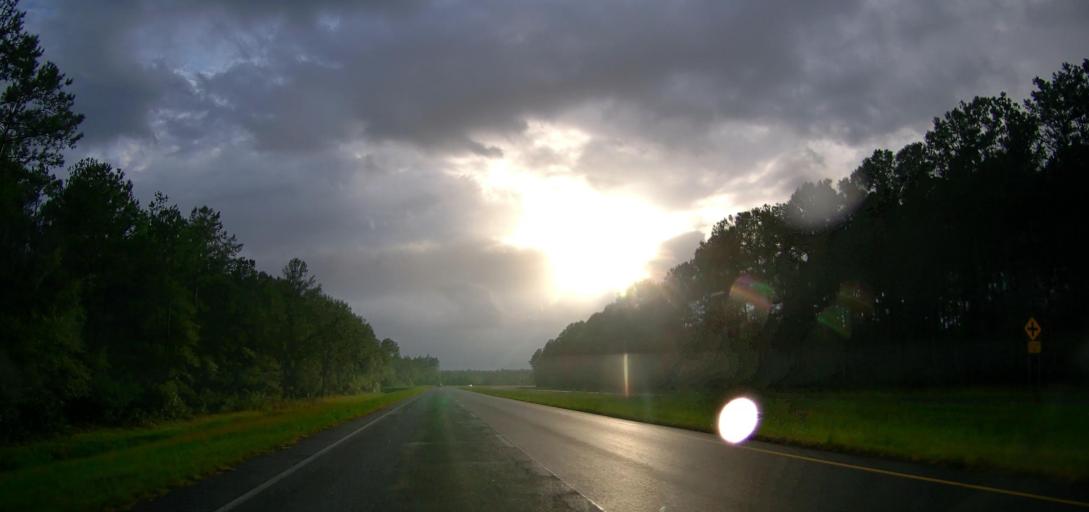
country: US
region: Georgia
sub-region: Ware County
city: Deenwood
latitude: 31.2092
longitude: -82.4080
